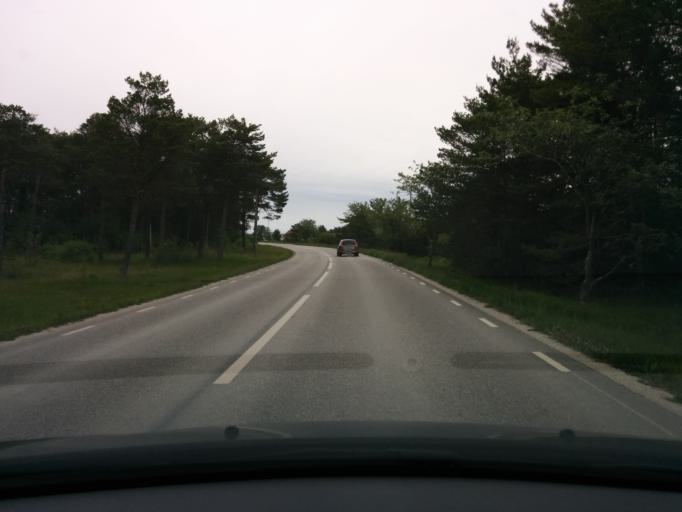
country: SE
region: Gotland
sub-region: Gotland
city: Slite
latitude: 57.6872
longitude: 18.7932
